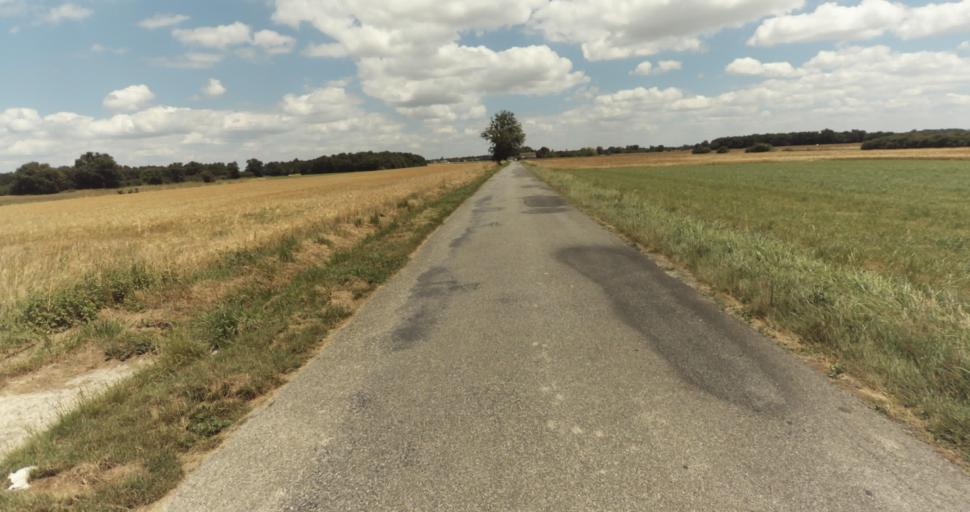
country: FR
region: Midi-Pyrenees
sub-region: Departement de la Haute-Garonne
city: Fontenilles
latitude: 43.5393
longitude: 1.1681
